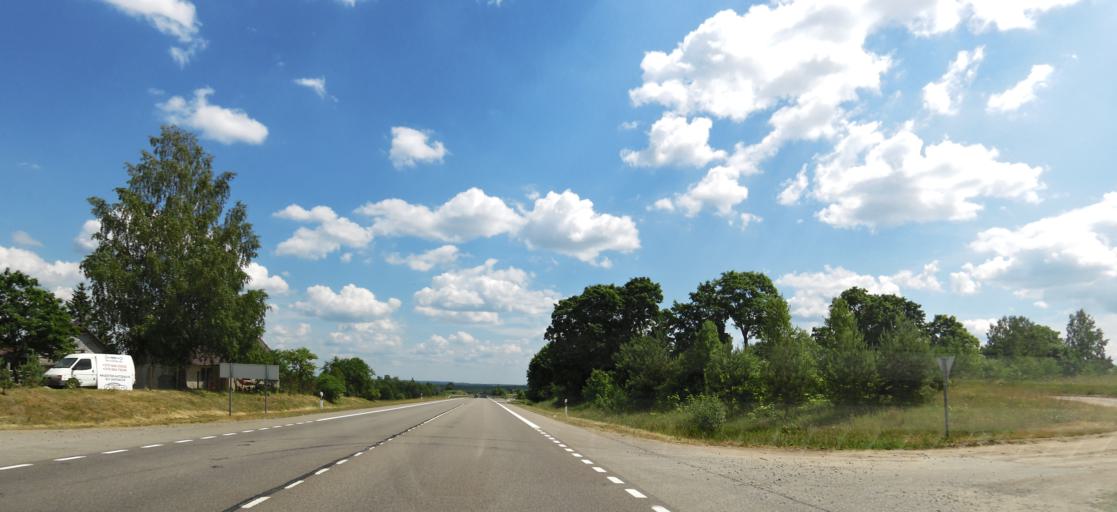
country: LT
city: Skaidiskes
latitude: 54.6042
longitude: 25.4757
